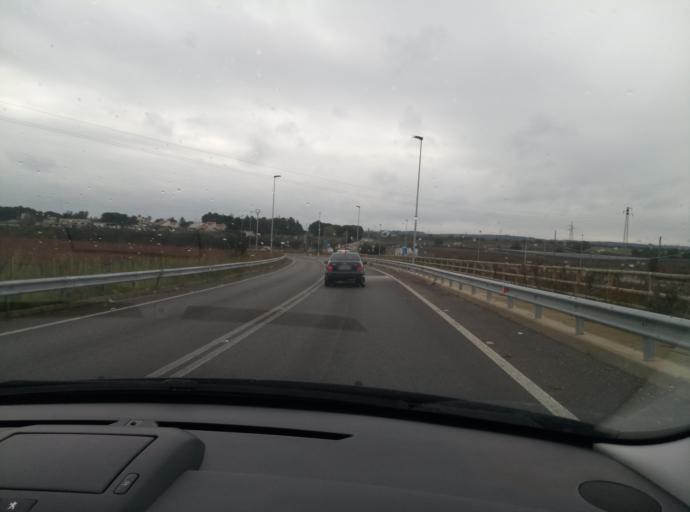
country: IT
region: Apulia
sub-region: Provincia di Bari
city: Acquaviva delle Fonti
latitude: 40.8839
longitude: 16.8130
